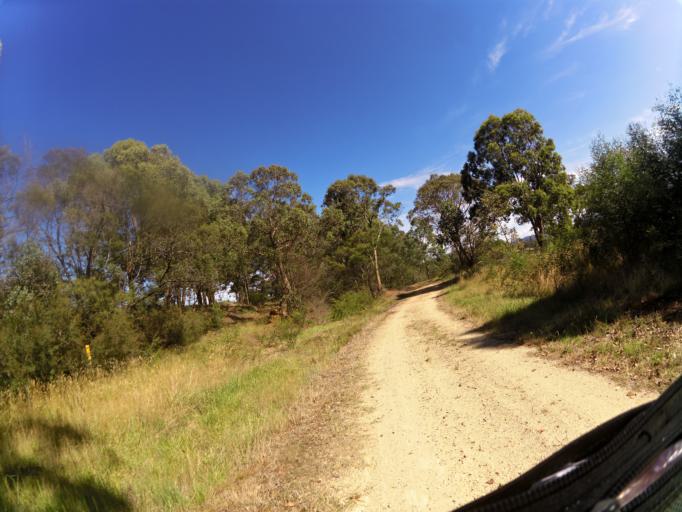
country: AU
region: Victoria
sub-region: East Gippsland
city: Lakes Entrance
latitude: -37.7357
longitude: 148.1650
